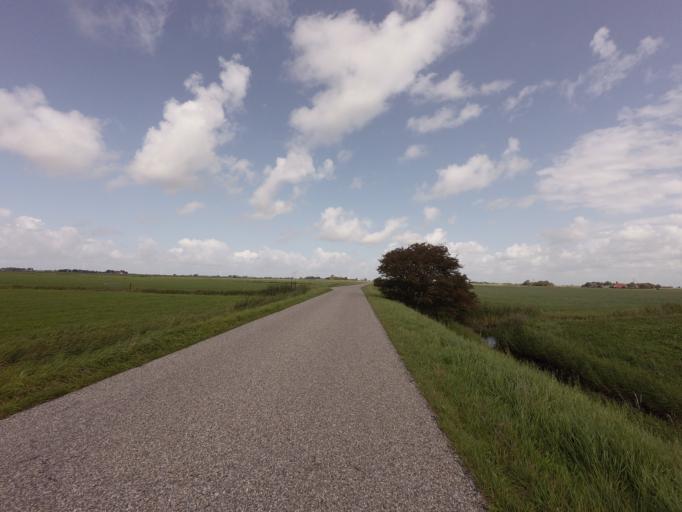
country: NL
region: Friesland
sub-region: Gemeente Franekeradeel
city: Sexbierum
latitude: 53.1619
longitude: 5.4843
